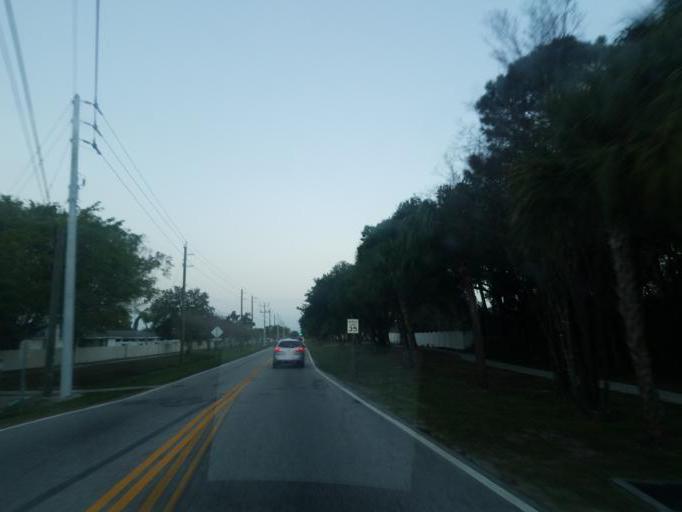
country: US
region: Florida
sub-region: Sarasota County
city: Fruitville
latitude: 27.3446
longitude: -82.4639
